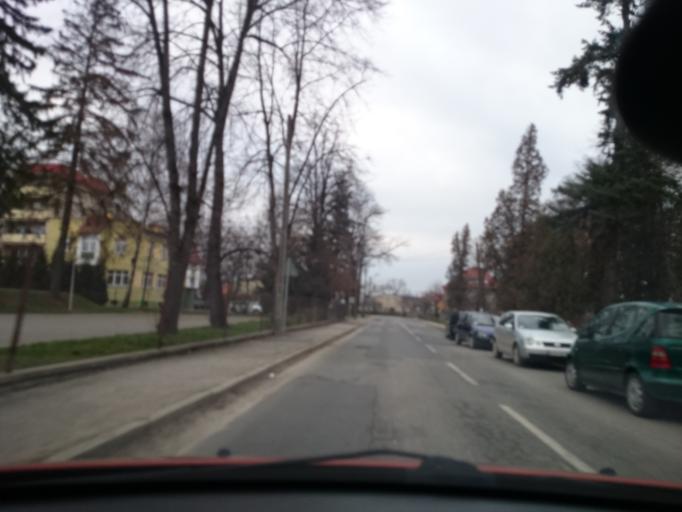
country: PL
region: Opole Voivodeship
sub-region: Powiat nyski
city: Paczkow
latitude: 50.4627
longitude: 17.0157
